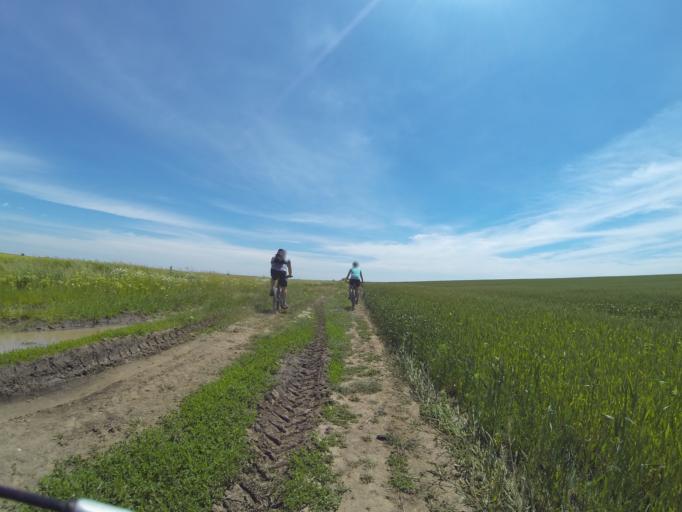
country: RO
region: Dolj
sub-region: Comuna Leu
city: Zanoaga
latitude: 44.1865
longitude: 24.0568
